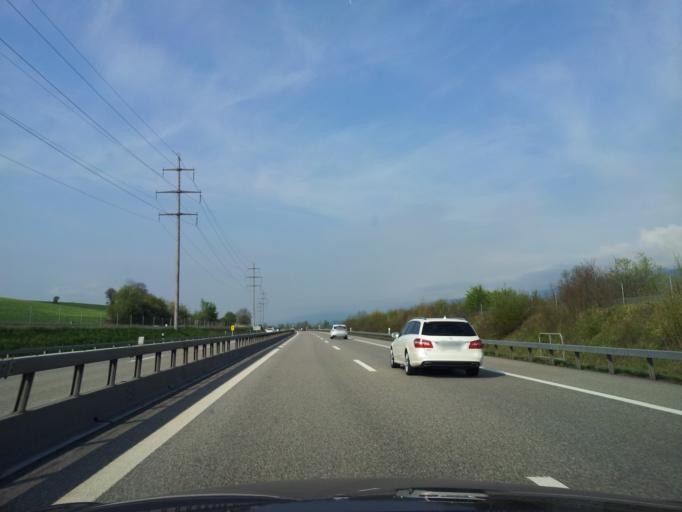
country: CH
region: Bern
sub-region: Seeland District
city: Leuzigen
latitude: 47.1892
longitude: 7.4801
